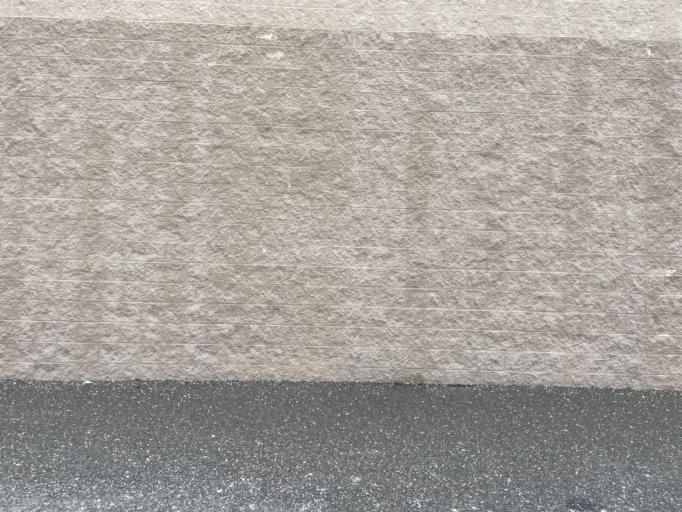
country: US
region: Massachusetts
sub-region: Bristol County
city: Fall River
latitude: 41.6941
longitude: -71.1402
